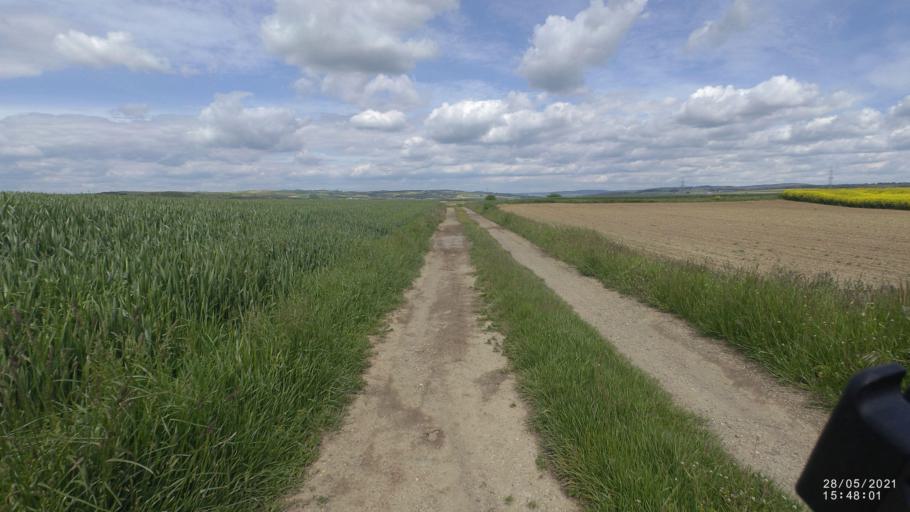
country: DE
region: Rheinland-Pfalz
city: Gappenach
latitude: 50.2687
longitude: 7.3326
